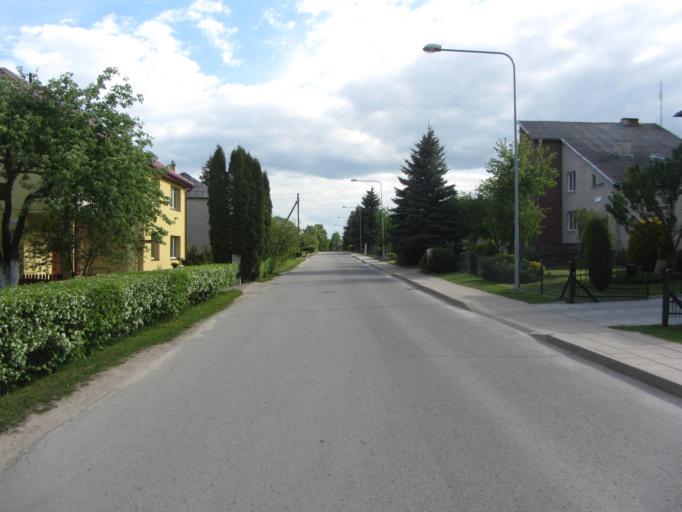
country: LT
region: Utenos apskritis
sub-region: Utena
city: Utena
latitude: 55.4900
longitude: 25.5978
